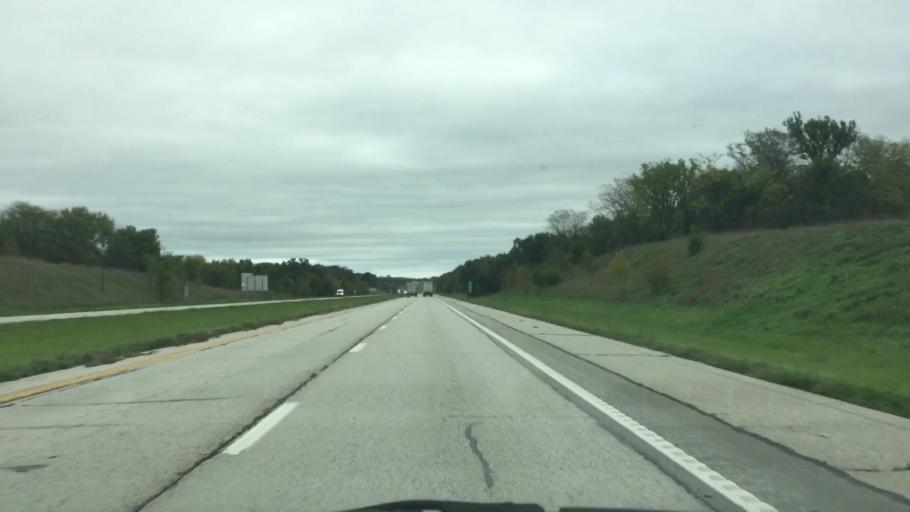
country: US
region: Missouri
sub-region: Harrison County
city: Bethany
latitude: 40.0904
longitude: -94.0849
